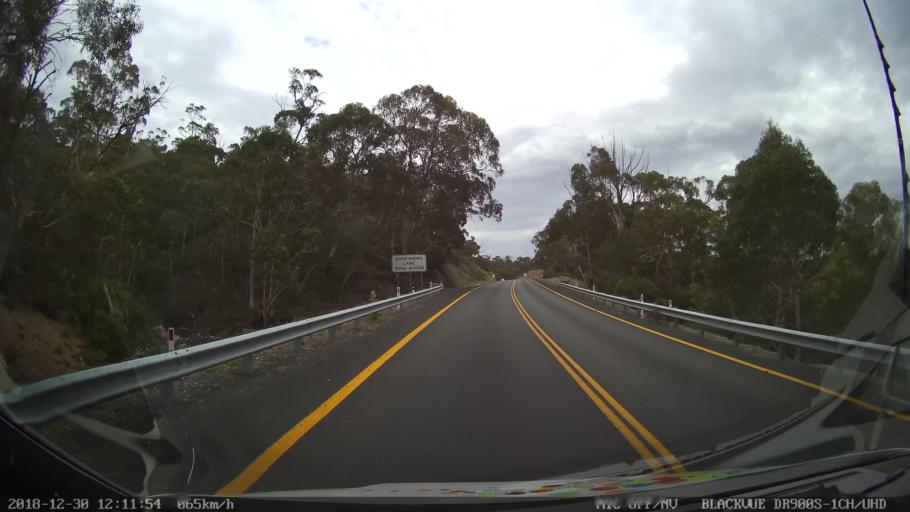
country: AU
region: New South Wales
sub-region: Snowy River
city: Jindabyne
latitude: -36.3622
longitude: 148.5870
